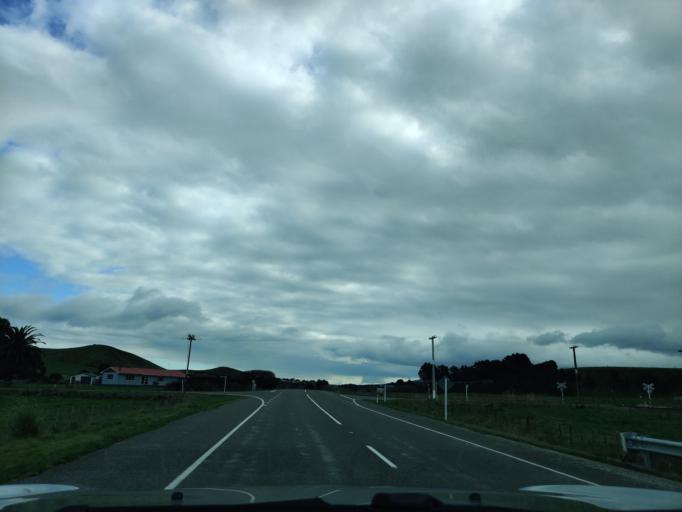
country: NZ
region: Manawatu-Wanganui
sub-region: Palmerston North City
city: Palmerston North
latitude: -40.2815
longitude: 175.9974
